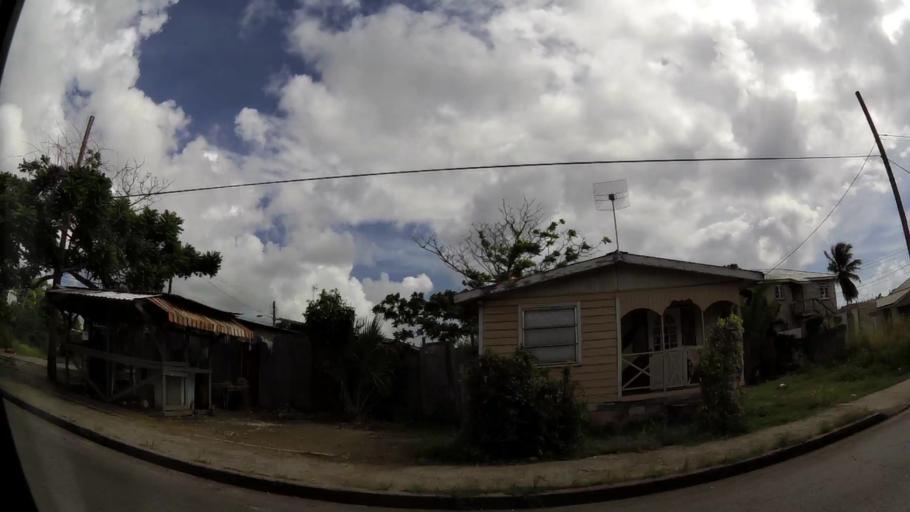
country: BB
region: Saint Michael
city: Bridgetown
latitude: 13.1093
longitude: -59.6185
